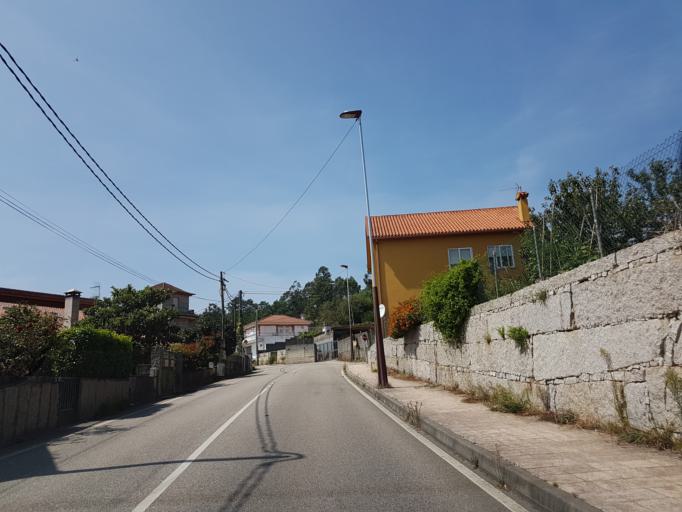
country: ES
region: Galicia
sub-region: Provincia de Pontevedra
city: Porrino
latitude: 42.2218
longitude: -8.6233
